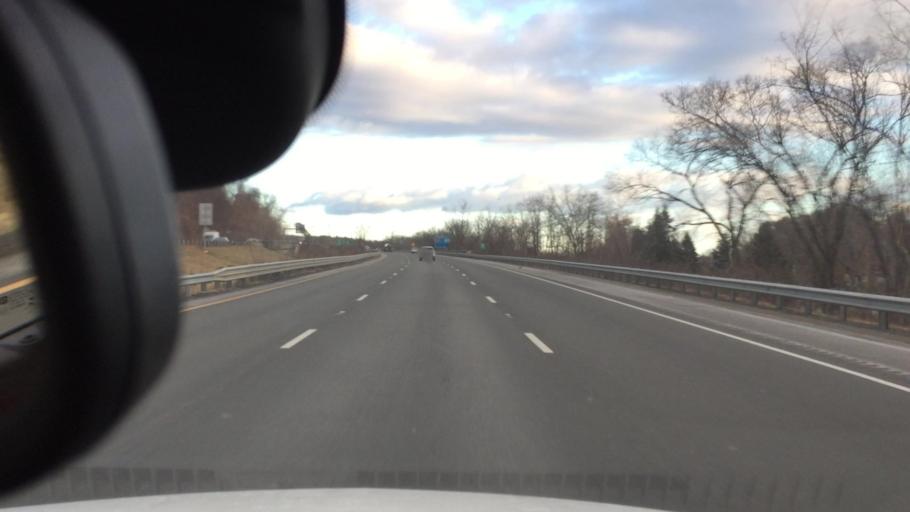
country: US
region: Massachusetts
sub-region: Hampden County
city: Holyoke
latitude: 42.1899
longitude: -72.6381
